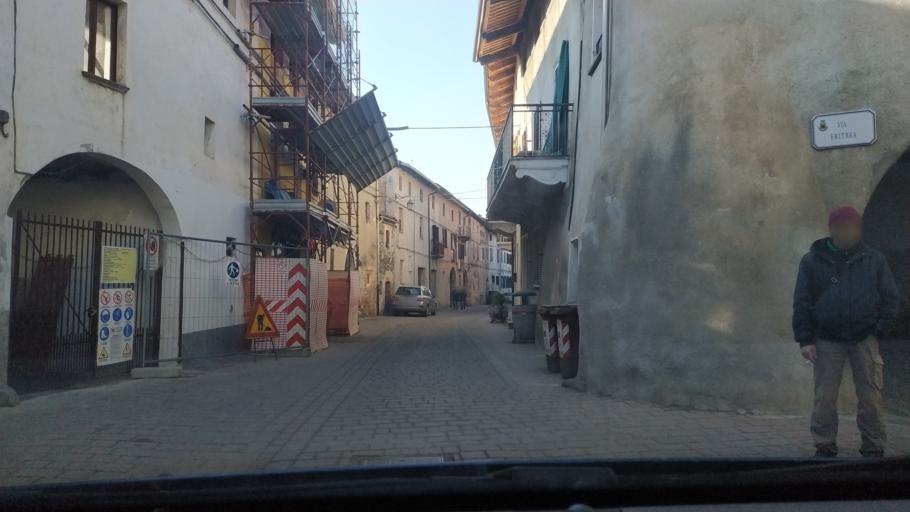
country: IT
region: Piedmont
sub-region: Provincia di Torino
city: Pavone Canavese
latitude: 45.4355
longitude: 7.8527
